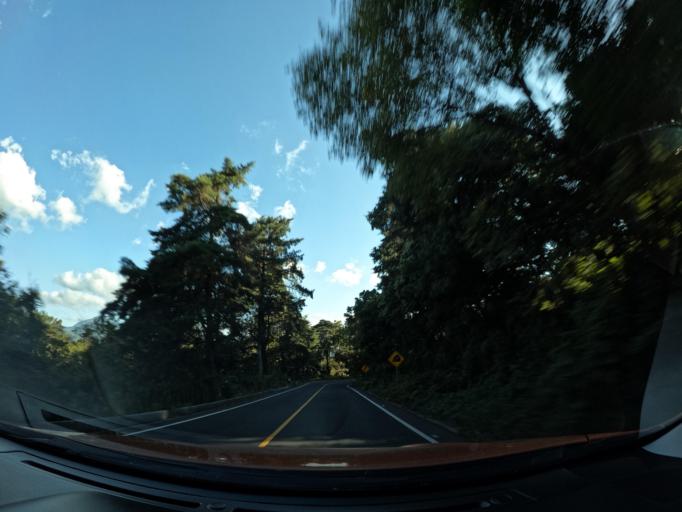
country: GT
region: Escuintla
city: Palin
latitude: 14.4415
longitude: -90.6942
